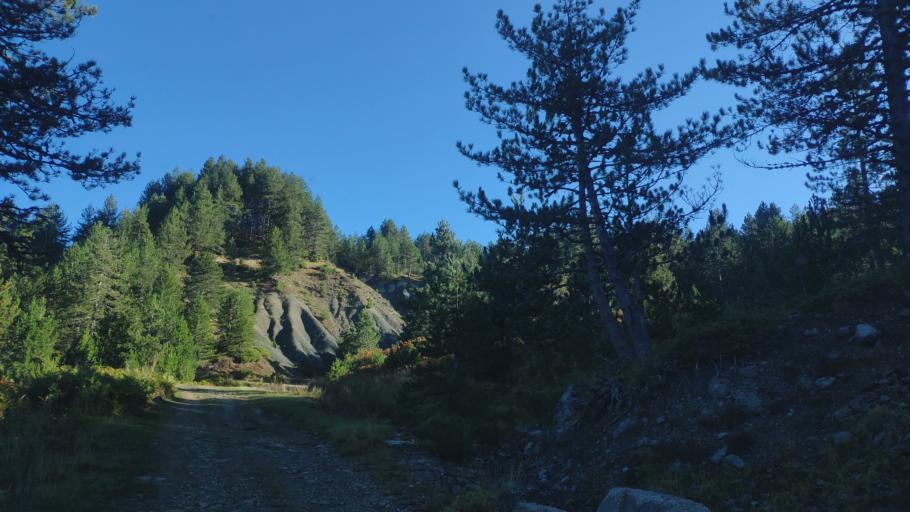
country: GR
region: Epirus
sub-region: Nomos Ioanninon
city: Metsovo
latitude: 39.8349
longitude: 21.1338
